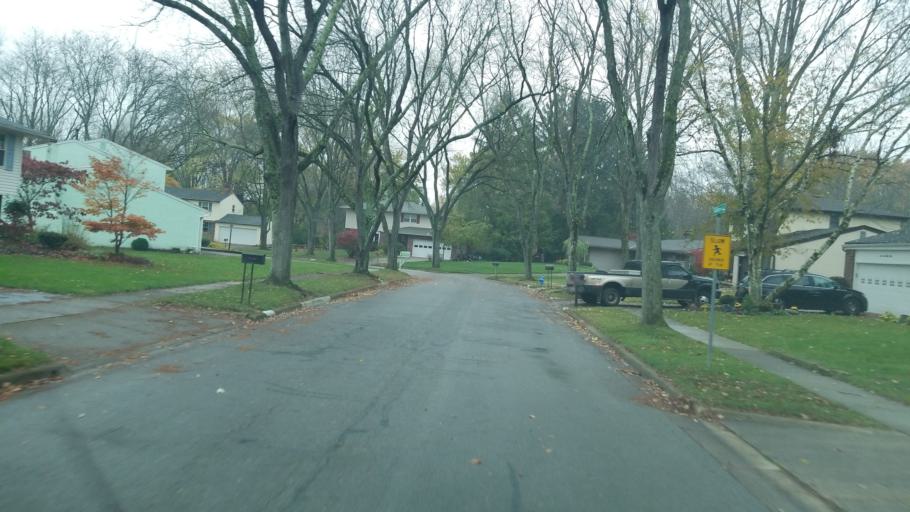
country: US
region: Ohio
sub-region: Franklin County
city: Worthington
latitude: 40.0865
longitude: -83.0430
